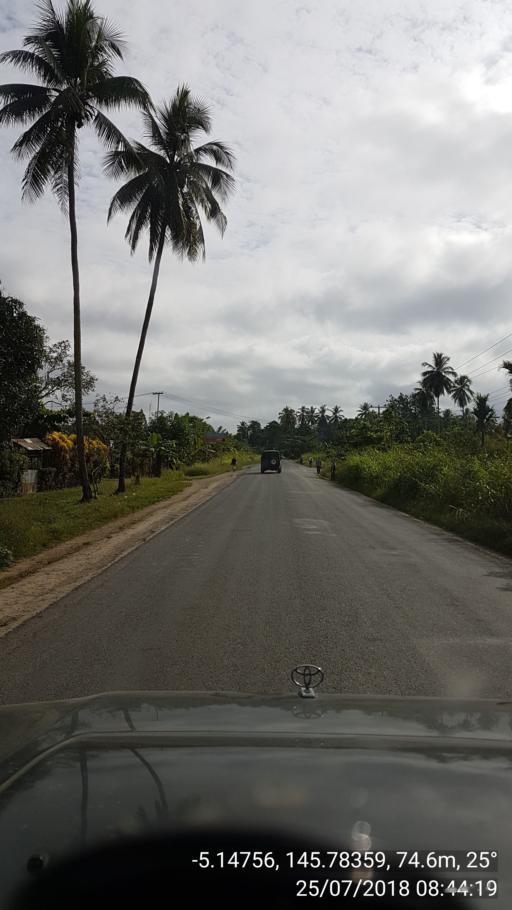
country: PG
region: Madang
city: Madang
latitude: -5.1478
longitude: 145.7836
